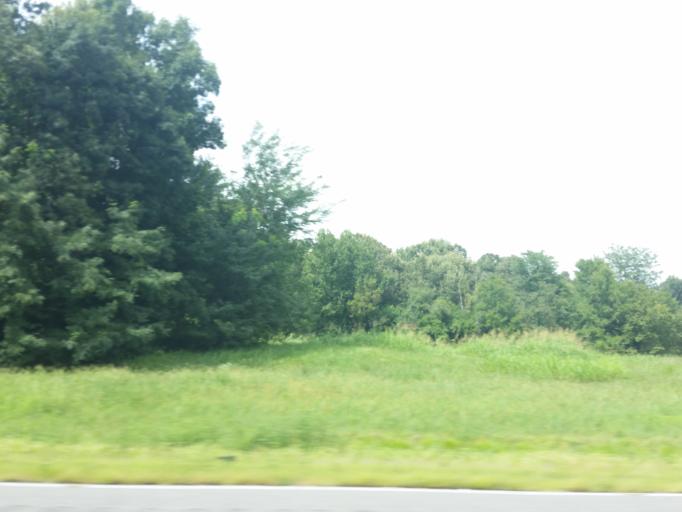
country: US
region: Kentucky
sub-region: Livingston County
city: Ledbetter
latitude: 36.9922
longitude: -88.4364
